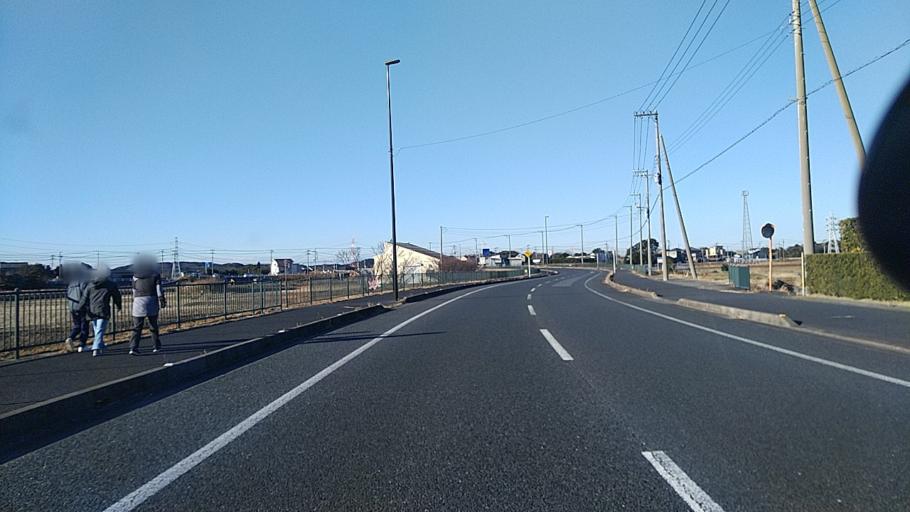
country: JP
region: Chiba
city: Kimitsu
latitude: 35.3224
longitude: 139.8869
